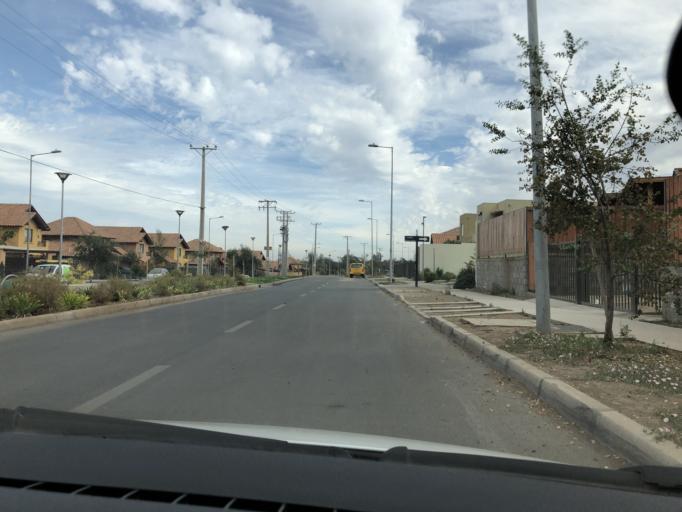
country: CL
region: Santiago Metropolitan
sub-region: Provincia de Cordillera
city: Puente Alto
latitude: -33.5835
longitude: -70.5142
